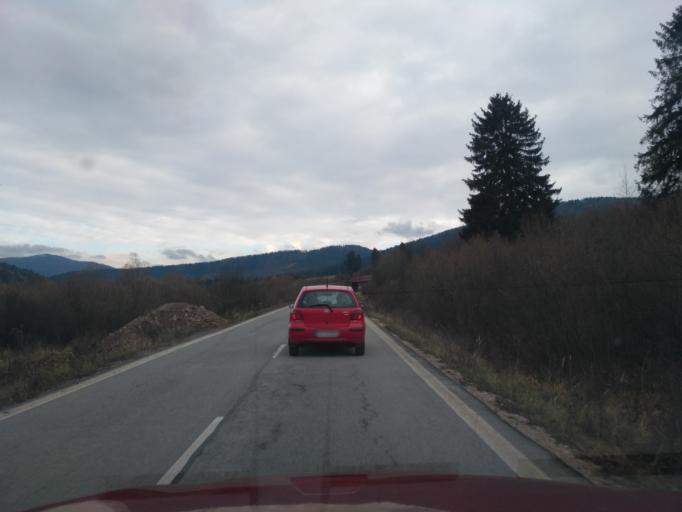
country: SK
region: Kosicky
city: Krompachy
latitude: 48.8045
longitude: 20.7283
